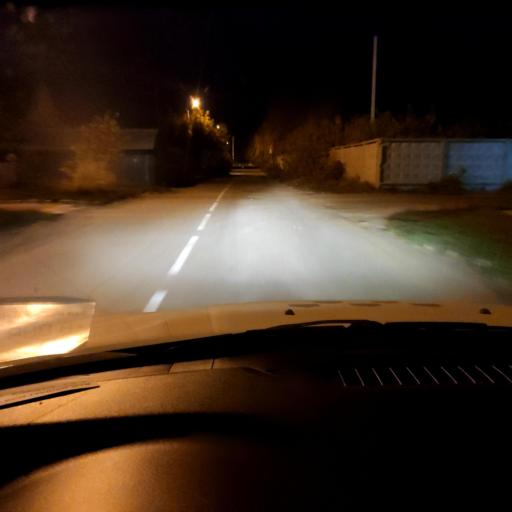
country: RU
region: Samara
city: Tol'yatti
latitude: 53.5395
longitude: 49.4250
